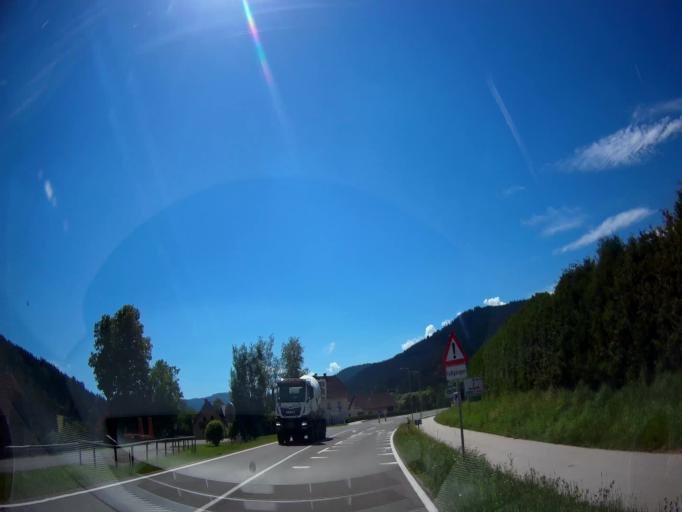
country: AT
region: Carinthia
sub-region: Politischer Bezirk Sankt Veit an der Glan
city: Gurk
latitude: 46.8630
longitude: 14.2356
